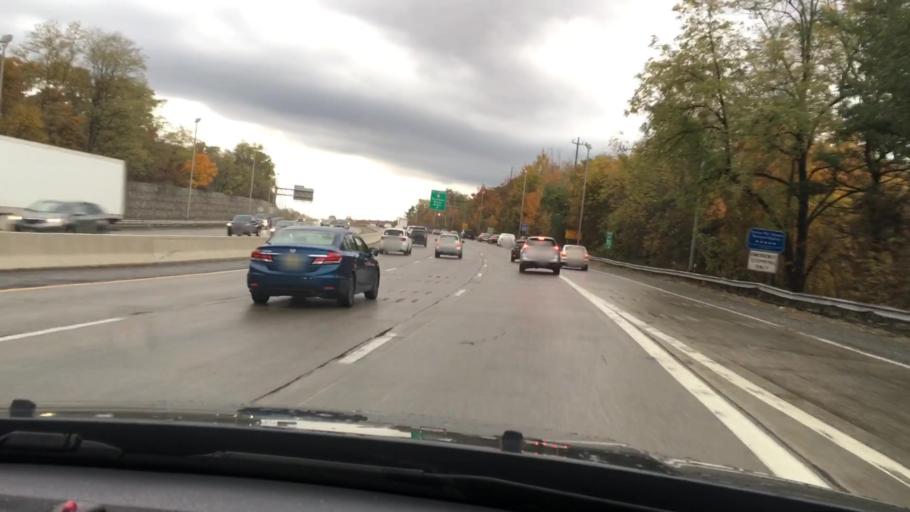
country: US
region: New Jersey
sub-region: Morris County
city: Riverdale
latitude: 40.9958
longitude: -74.3092
